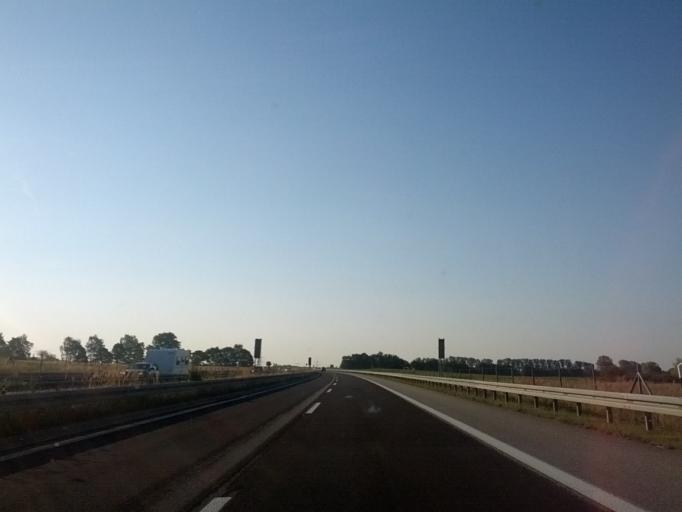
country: DE
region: Mecklenburg-Vorpommern
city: Wendorf
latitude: 54.2617
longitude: 13.0946
